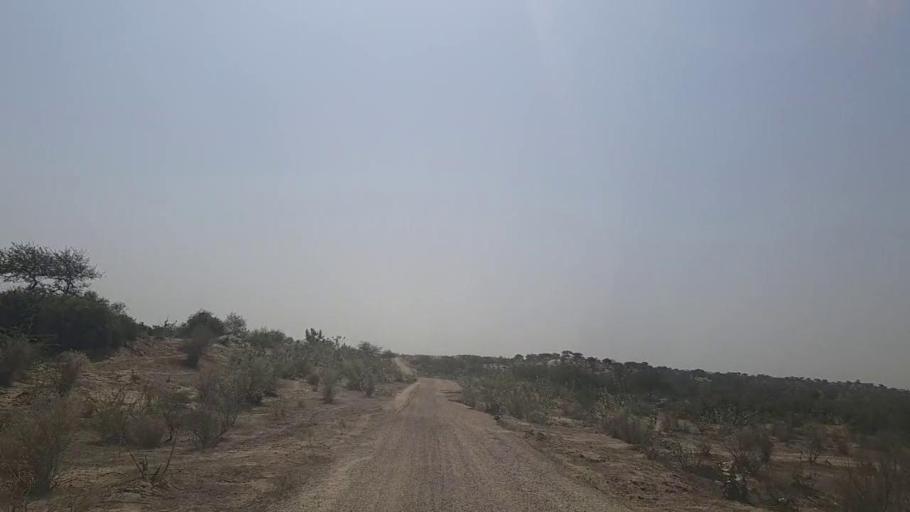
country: PK
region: Sindh
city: Naukot
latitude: 24.8120
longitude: 69.4745
